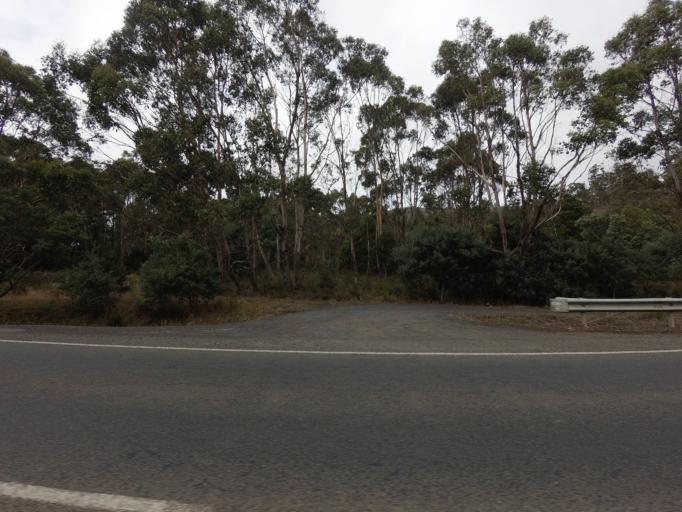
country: AU
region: Tasmania
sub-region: Derwent Valley
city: New Norfolk
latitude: -42.6826
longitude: 146.7360
